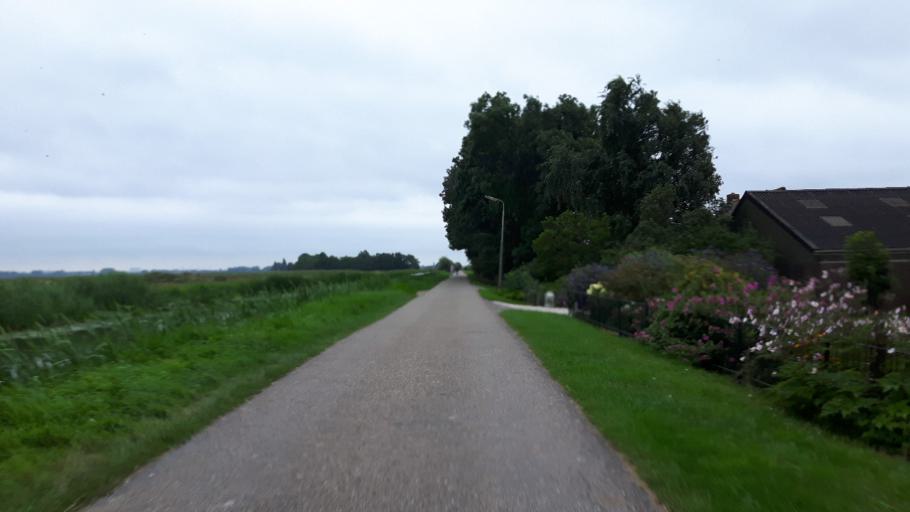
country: NL
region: South Holland
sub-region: Gemeente Alphen aan den Rijn
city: Alphen aan den Rijn
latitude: 52.1606
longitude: 4.6061
